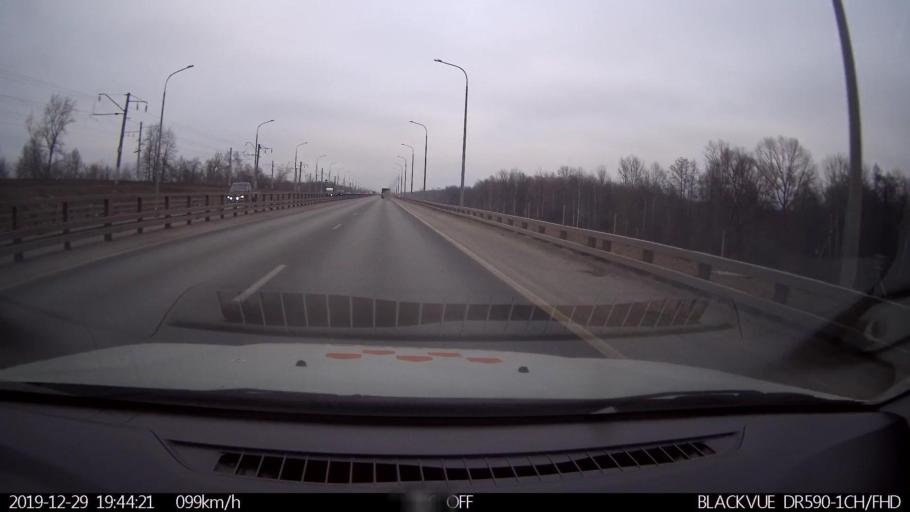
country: RU
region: Nizjnij Novgorod
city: Neklyudovo
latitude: 56.3735
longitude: 43.9488
